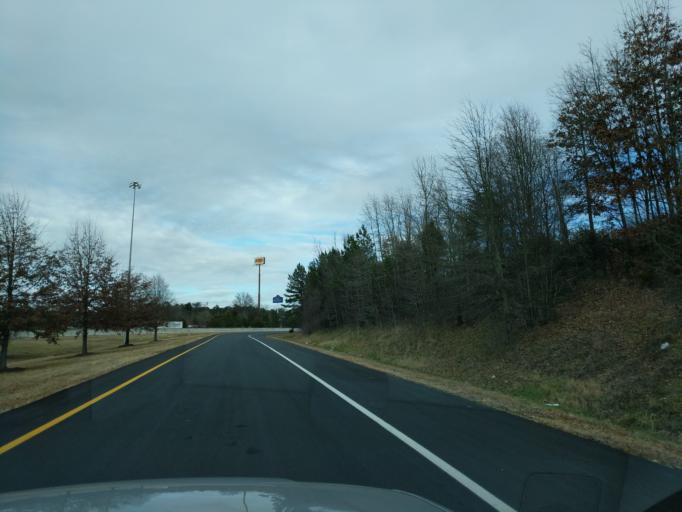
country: US
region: South Carolina
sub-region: Anderson County
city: Northlake
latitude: 34.5716
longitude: -82.7100
